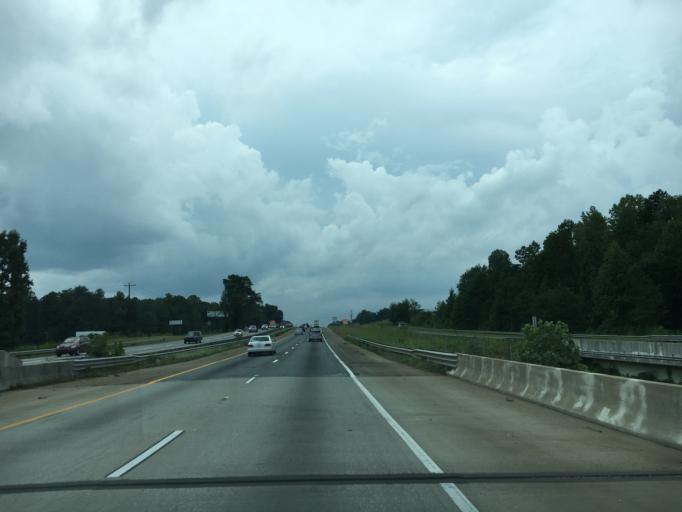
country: US
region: South Carolina
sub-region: Spartanburg County
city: Cowpens
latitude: 35.0330
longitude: -81.8503
